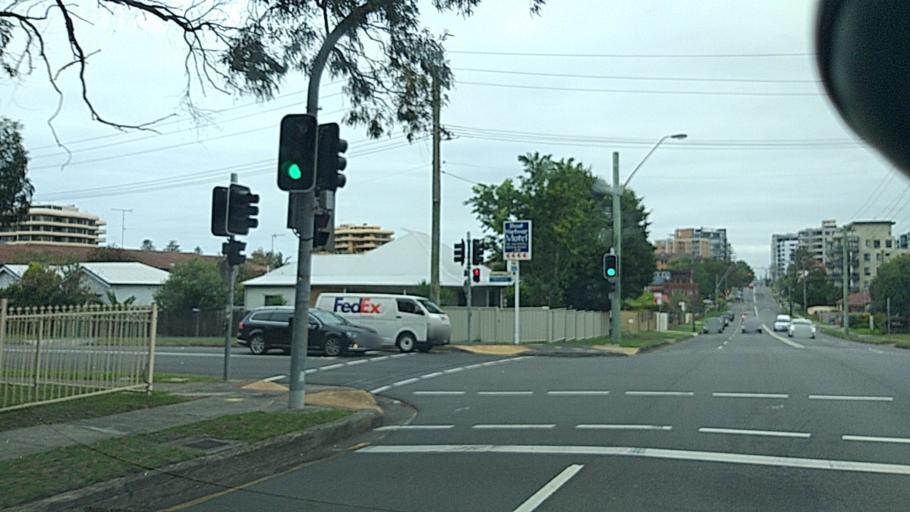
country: AU
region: New South Wales
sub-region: Wollongong
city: Wollongong
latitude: -34.4204
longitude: 150.9010
